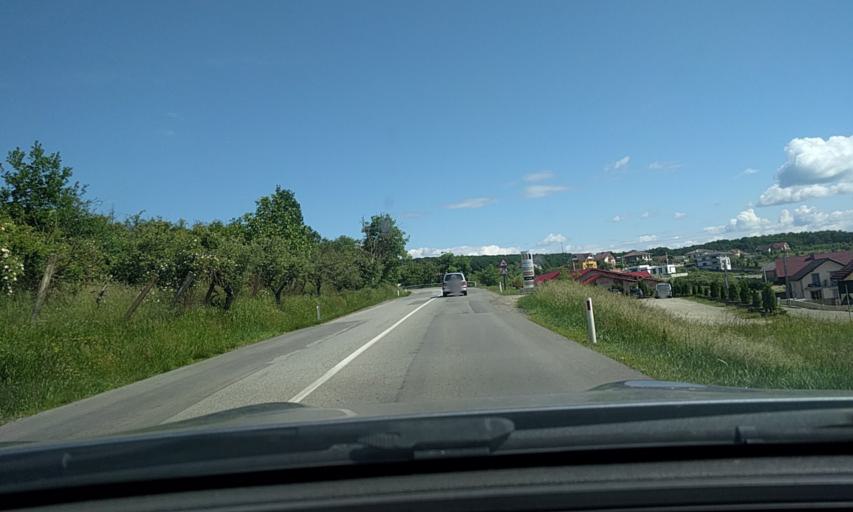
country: RO
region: Bistrita-Nasaud
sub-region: Municipiul Bistrita
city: Unirea
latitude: 47.1587
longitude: 24.5089
